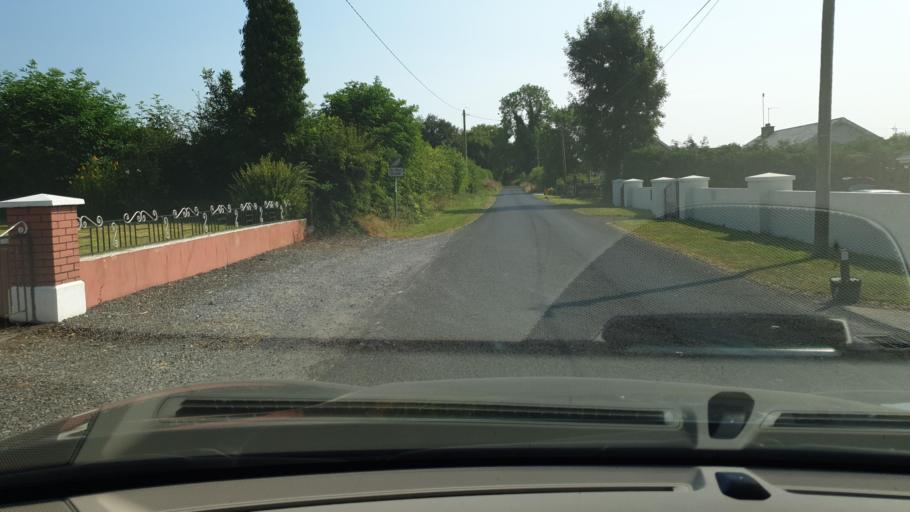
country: IE
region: Leinster
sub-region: An Mhi
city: Ballivor
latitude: 53.6045
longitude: -6.9958
